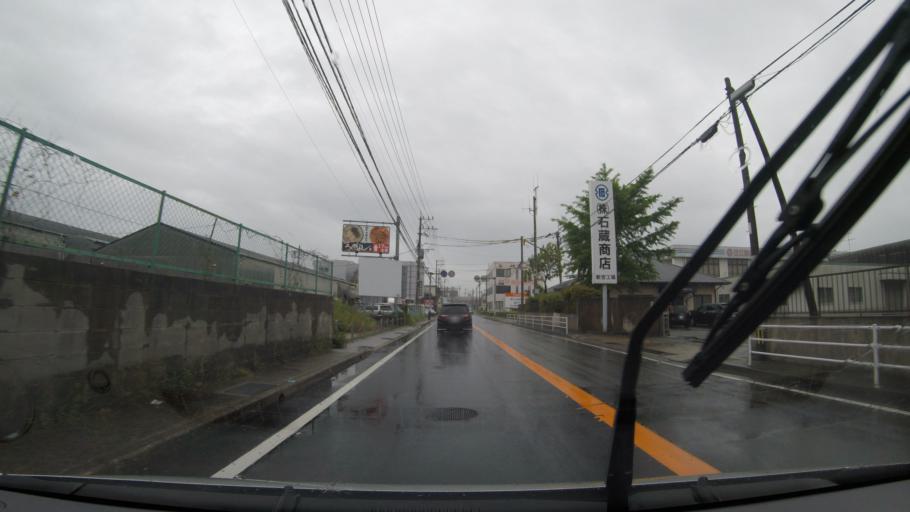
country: JP
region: Fukuoka
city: Koga
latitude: 33.7192
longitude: 130.4536
